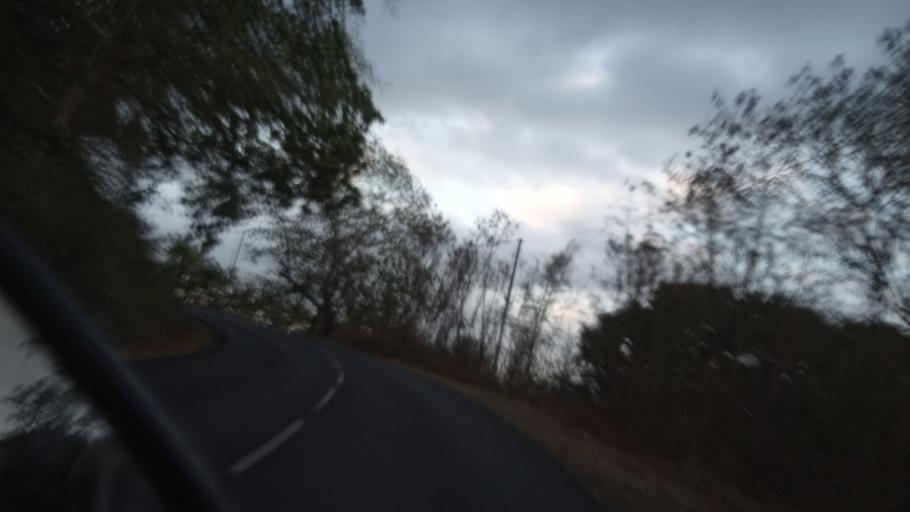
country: YT
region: Kani-Keli
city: Kani Keli
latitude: -12.9302
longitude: 45.1183
